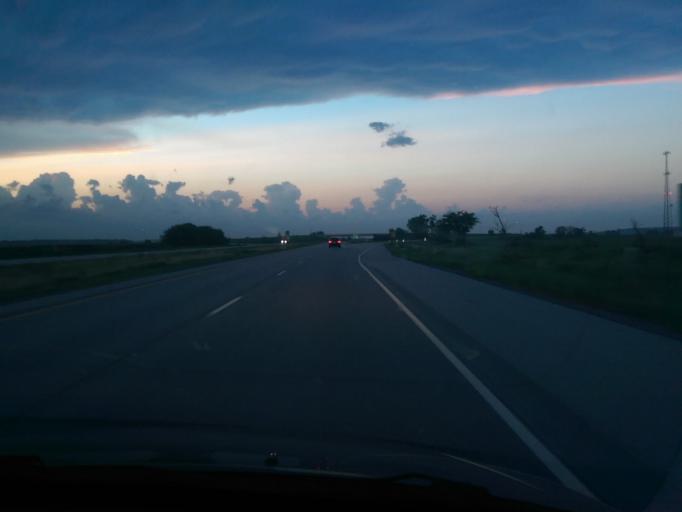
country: US
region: Nebraska
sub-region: Otoe County
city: Nebraska City
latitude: 40.7521
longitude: -95.8174
